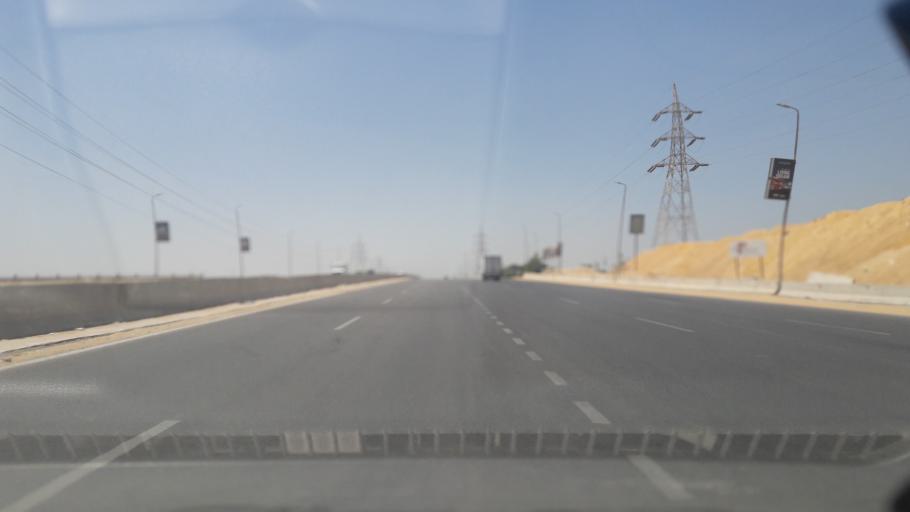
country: EG
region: Al Jizah
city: Al Jizah
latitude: 30.0036
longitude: 31.0891
